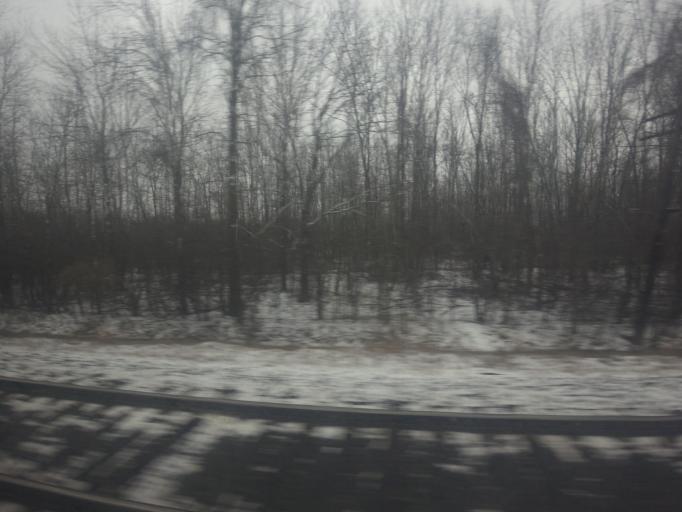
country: CA
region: Ontario
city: Quinte West
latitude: 44.1467
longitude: -77.4951
